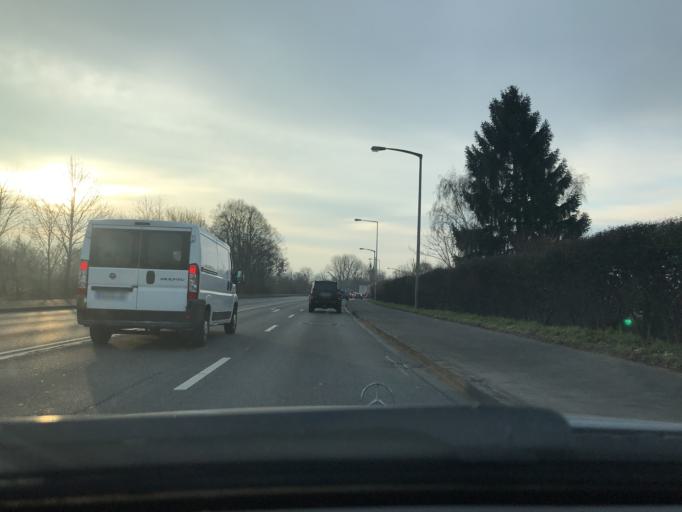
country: DE
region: Hesse
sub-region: Regierungsbezirk Kassel
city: Kassel
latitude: 51.3053
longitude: 9.5151
